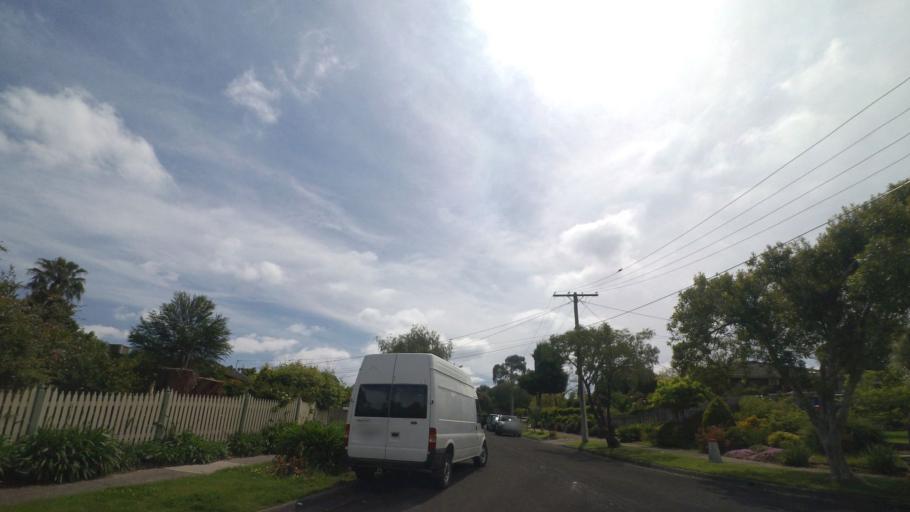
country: AU
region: Victoria
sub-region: Knox
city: Bayswater
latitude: -37.8526
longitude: 145.2494
